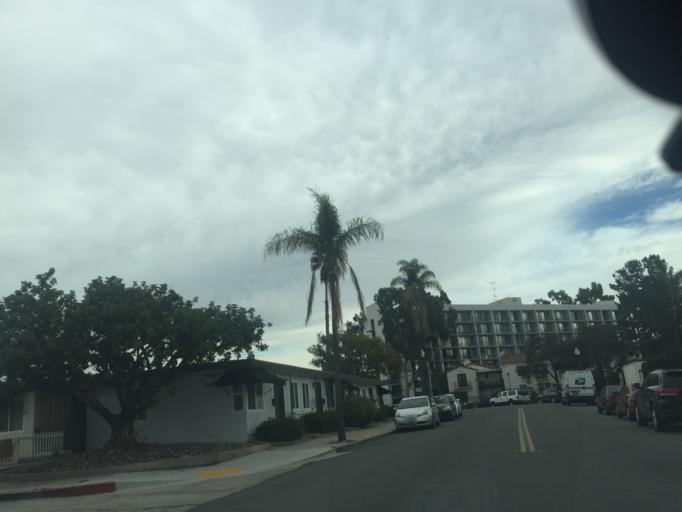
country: US
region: California
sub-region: San Diego County
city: Lemon Grove
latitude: 32.7590
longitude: -117.0826
